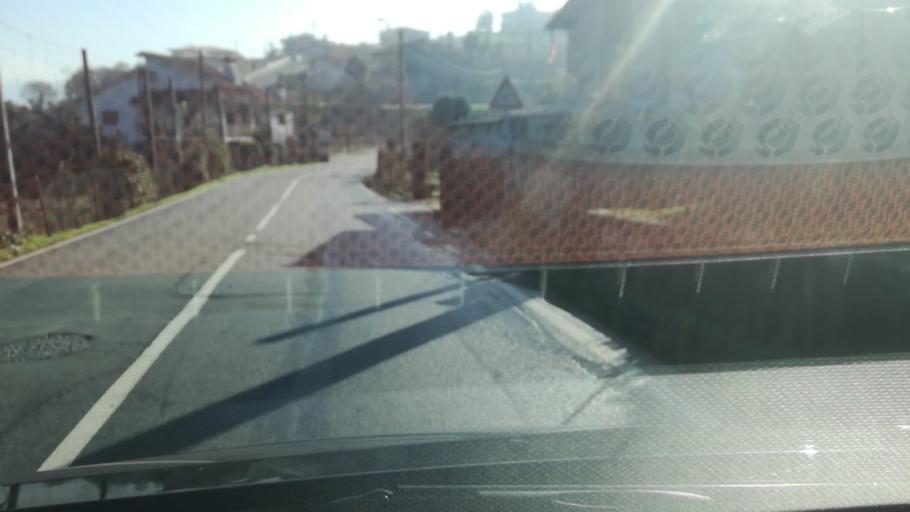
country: PT
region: Braga
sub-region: Guimaraes
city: Ponte
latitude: 41.5211
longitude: -8.3400
